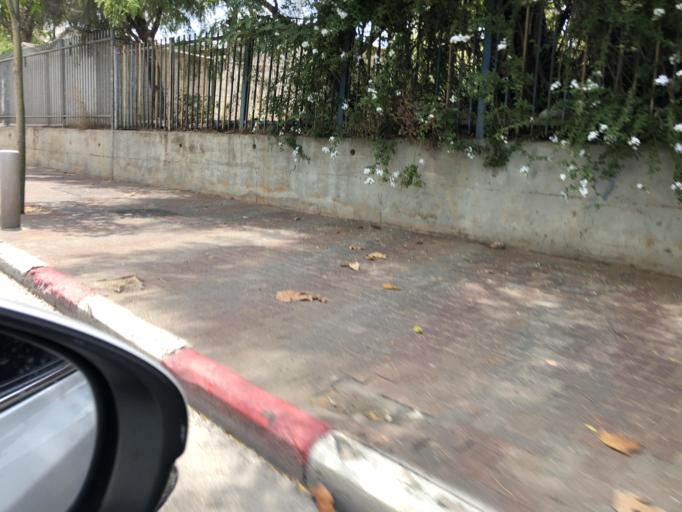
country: IL
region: Tel Aviv
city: Bene Beraq
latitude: 32.0644
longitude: 34.8329
